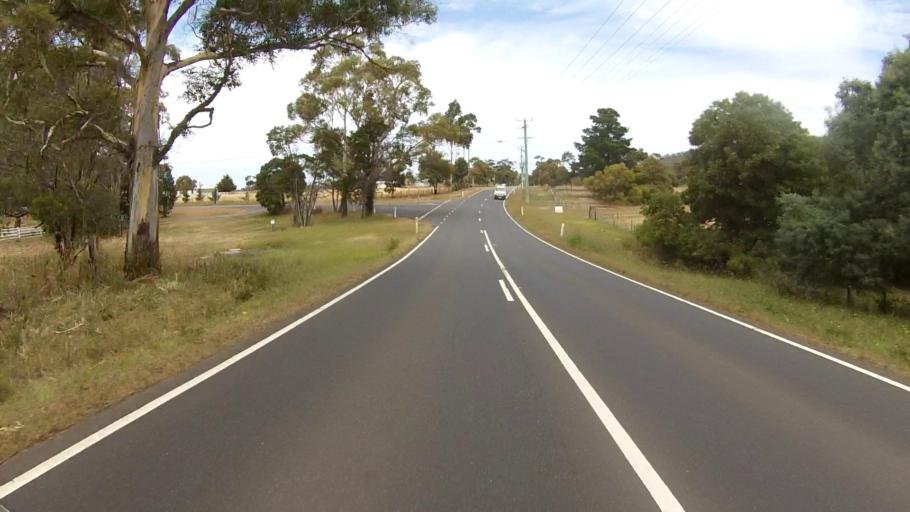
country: AU
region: Tasmania
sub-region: Clarence
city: Acton Park
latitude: -42.8874
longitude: 147.4830
